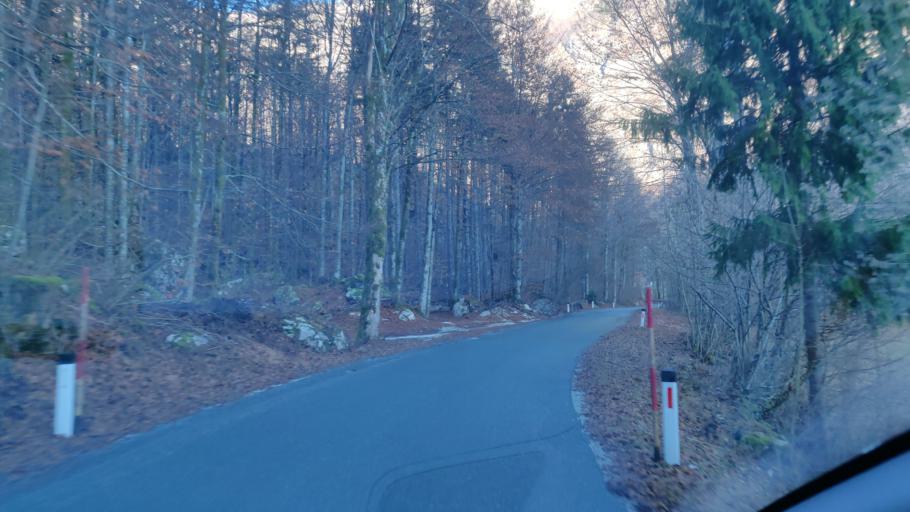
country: SI
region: Tolmin
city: Tolmin
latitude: 46.2798
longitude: 13.8098
